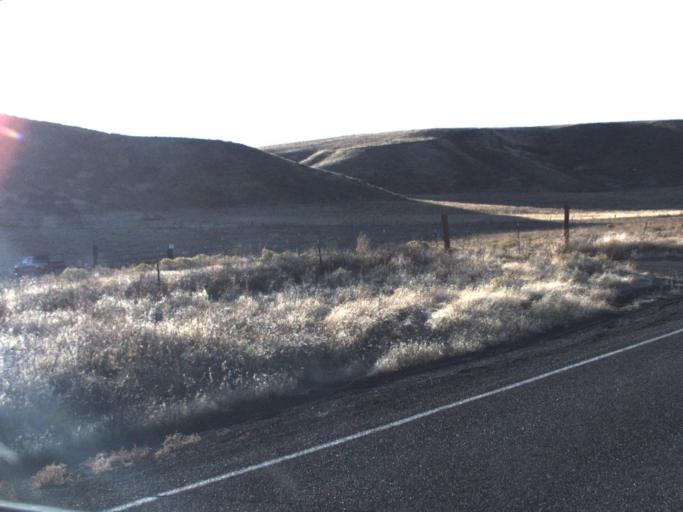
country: US
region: Washington
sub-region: Walla Walla County
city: Waitsburg
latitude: 46.6265
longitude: -118.2385
